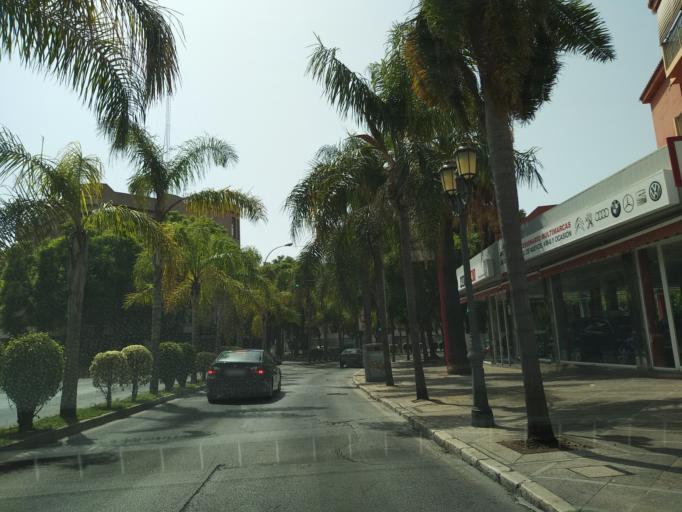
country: ES
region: Andalusia
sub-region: Provincia de Malaga
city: Torremolinos
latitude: 36.6194
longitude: -4.4997
